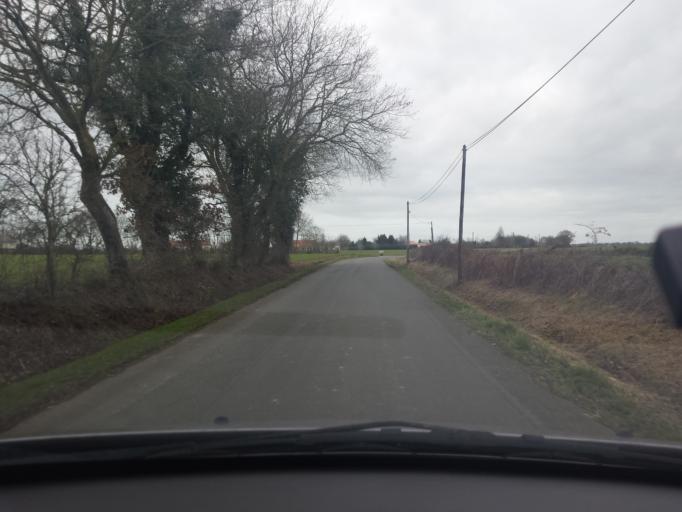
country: FR
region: Pays de la Loire
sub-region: Departement de la Vendee
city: Les Essarts
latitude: 46.7608
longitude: -1.2609
